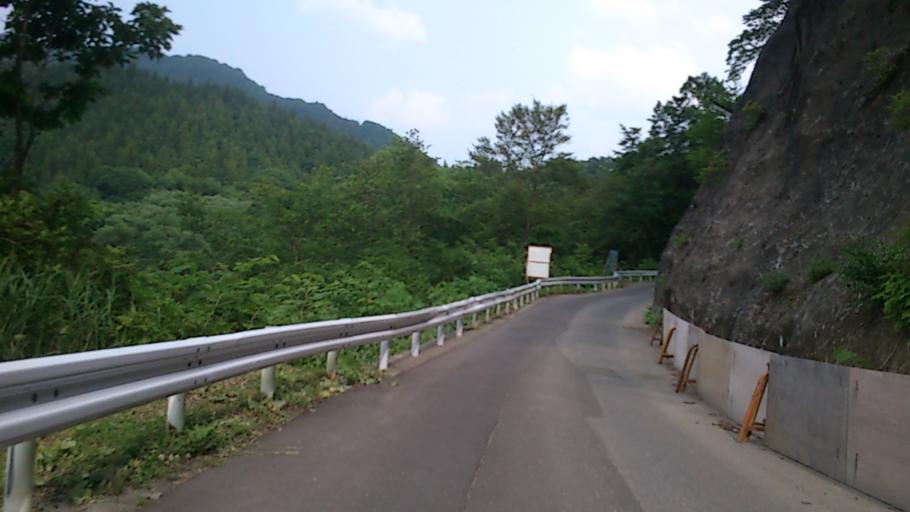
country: JP
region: Aomori
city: Hirosaki
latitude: 40.5201
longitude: 140.1768
